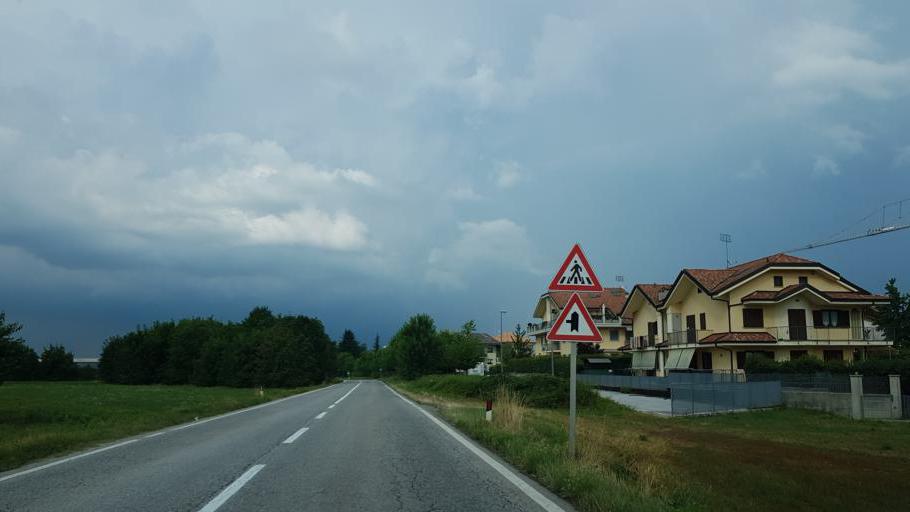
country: IT
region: Piedmont
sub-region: Provincia di Cuneo
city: Borgo San Dalmazzo
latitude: 44.3342
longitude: 7.4767
